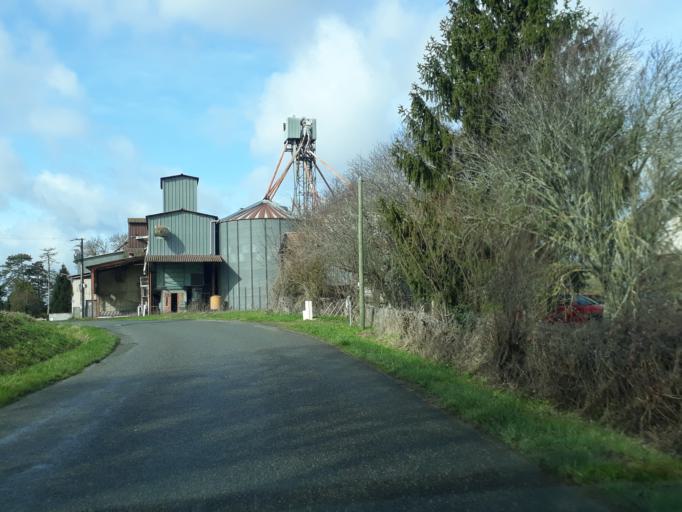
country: FR
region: Midi-Pyrenees
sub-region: Departement du Gers
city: Gimont
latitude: 43.6400
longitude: 1.0010
